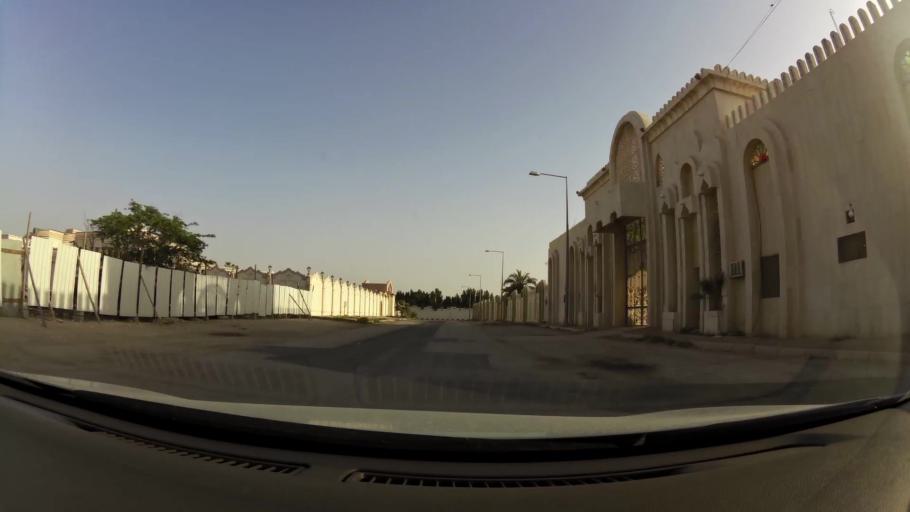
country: QA
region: Baladiyat ar Rayyan
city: Ar Rayyan
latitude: 25.3321
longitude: 51.4523
